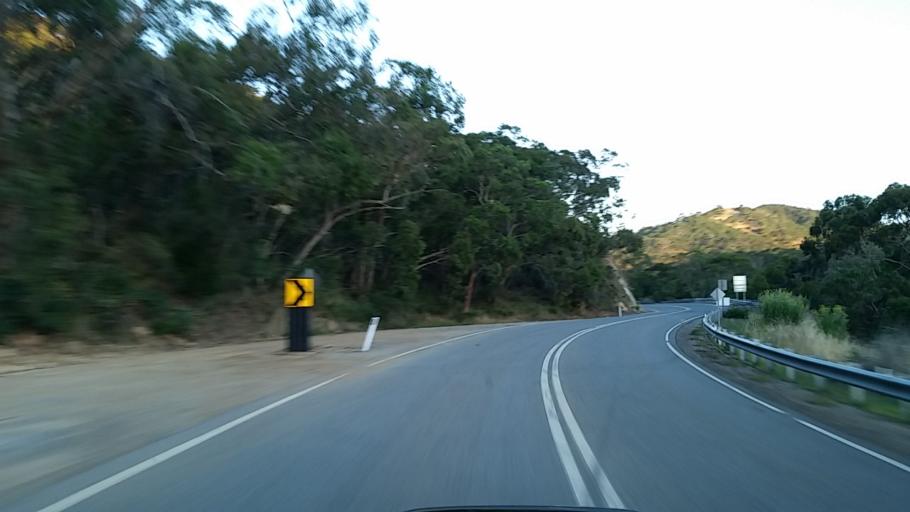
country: AU
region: South Australia
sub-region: Campbelltown
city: Athelstone
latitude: -34.8641
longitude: 138.7772
